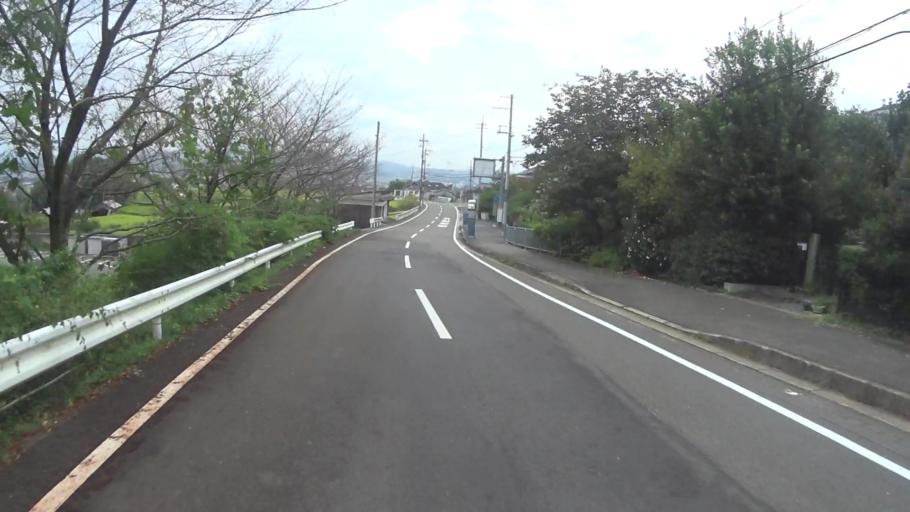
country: JP
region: Kyoto
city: Tanabe
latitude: 34.8020
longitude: 135.8201
